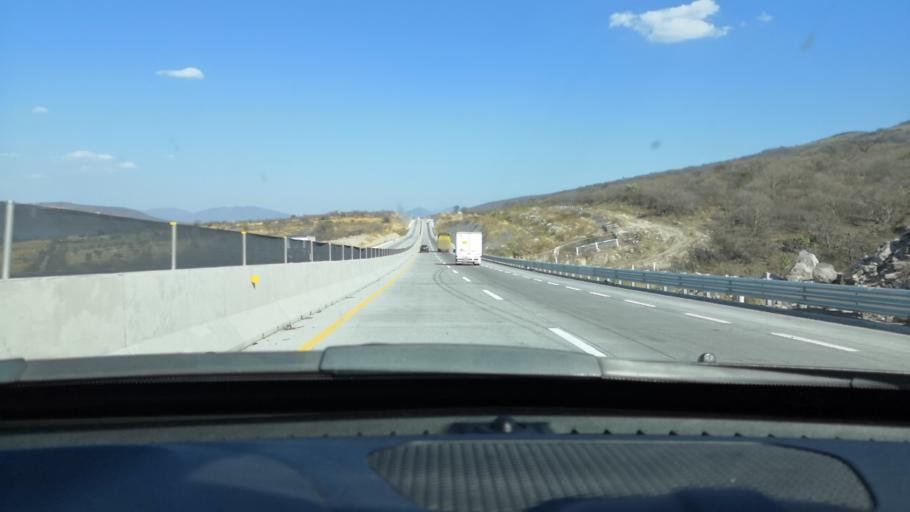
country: MX
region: Jalisco
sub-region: Tlajomulco de Zuniga
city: San Lucas Evangelista
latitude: 20.3917
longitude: -103.3299
